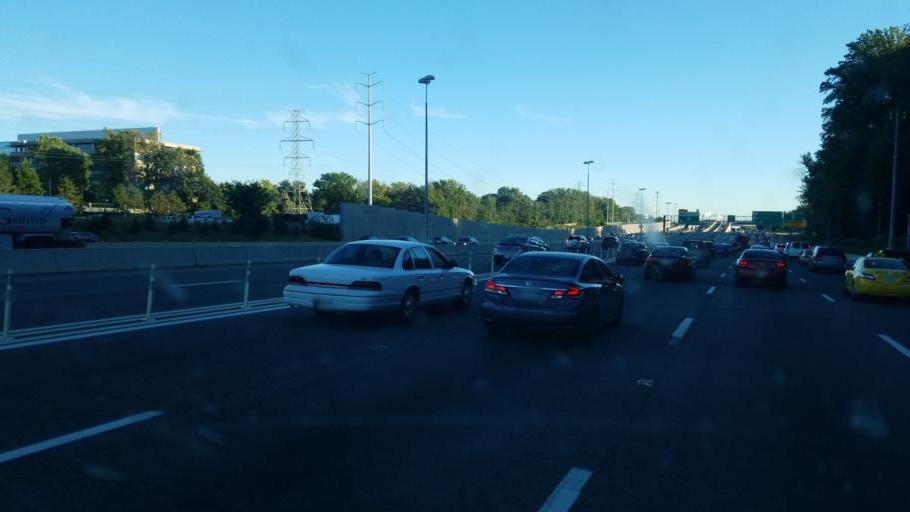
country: US
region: Virginia
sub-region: Fairfax County
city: Merrifield
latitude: 38.8610
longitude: -77.2204
